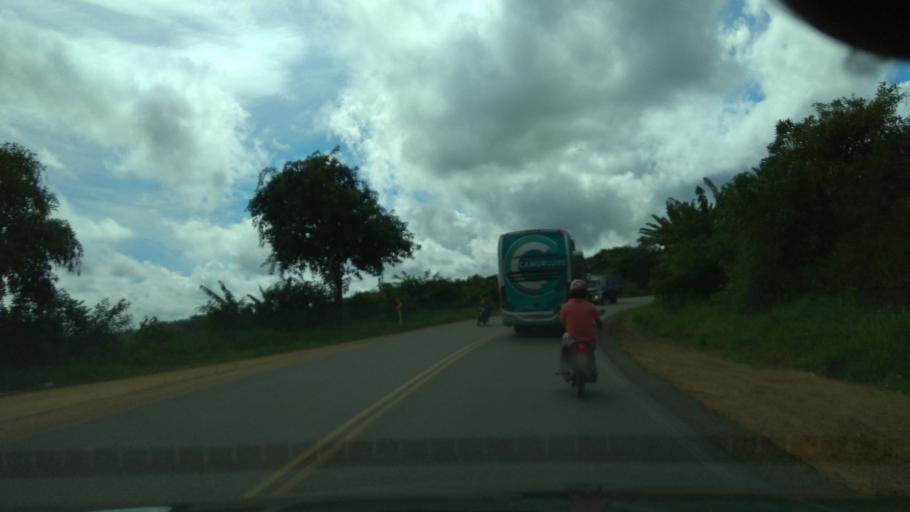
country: BR
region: Bahia
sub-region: Mutuipe
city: Mutuipe
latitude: -13.2134
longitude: -39.4808
